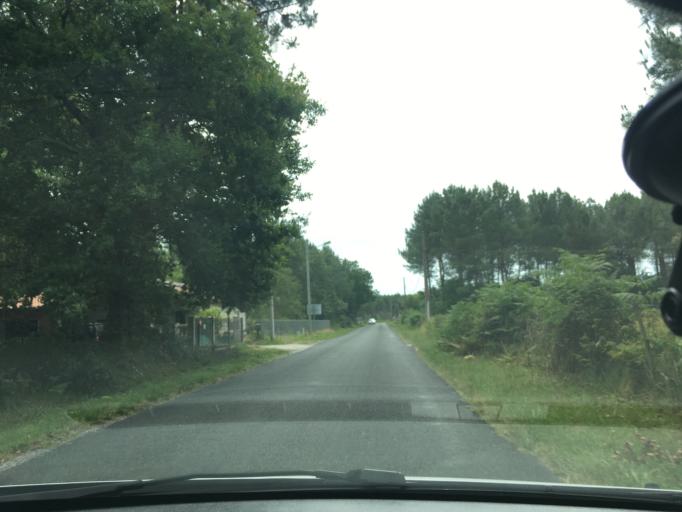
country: FR
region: Aquitaine
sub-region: Departement de la Gironde
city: Gaillan-en-Medoc
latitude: 45.3539
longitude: -1.0525
